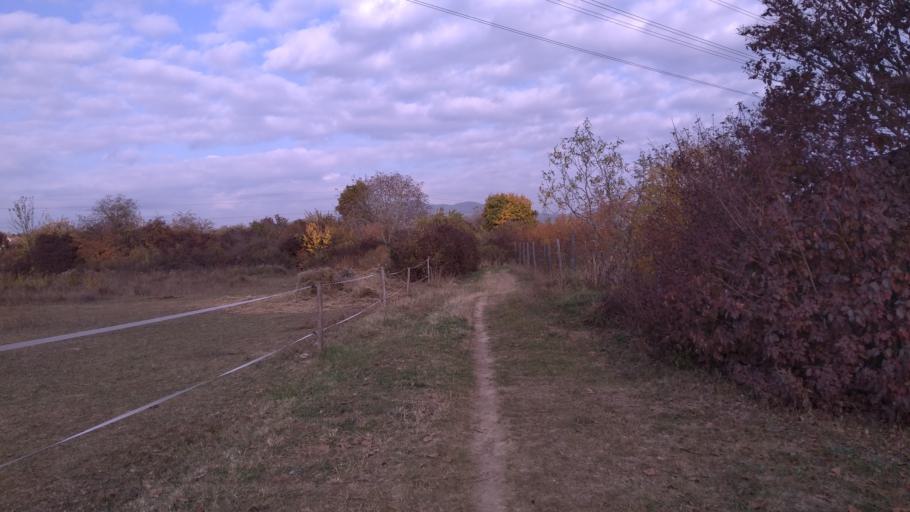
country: HU
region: Pest
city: Pomaz
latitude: 47.6301
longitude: 19.0358
